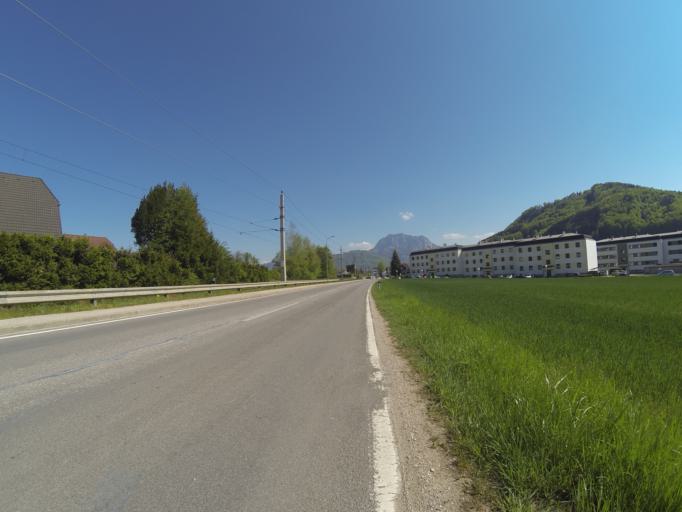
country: AT
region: Upper Austria
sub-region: Politischer Bezirk Gmunden
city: Altmunster
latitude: 47.9346
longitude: 13.7640
